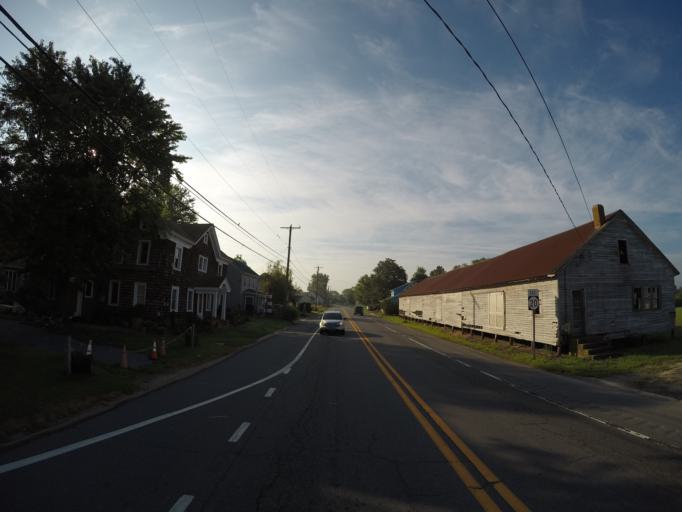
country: US
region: Delaware
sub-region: Sussex County
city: Selbyville
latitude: 38.4962
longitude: -75.1704
